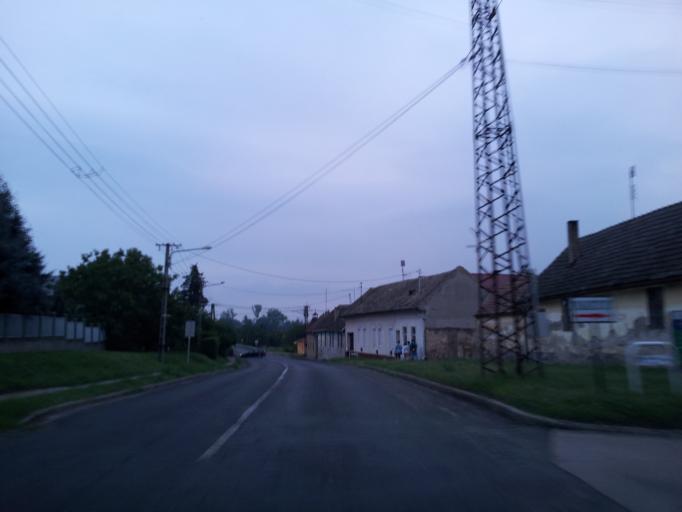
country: HU
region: Tolna
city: Tolna
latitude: 46.4245
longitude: 18.7919
